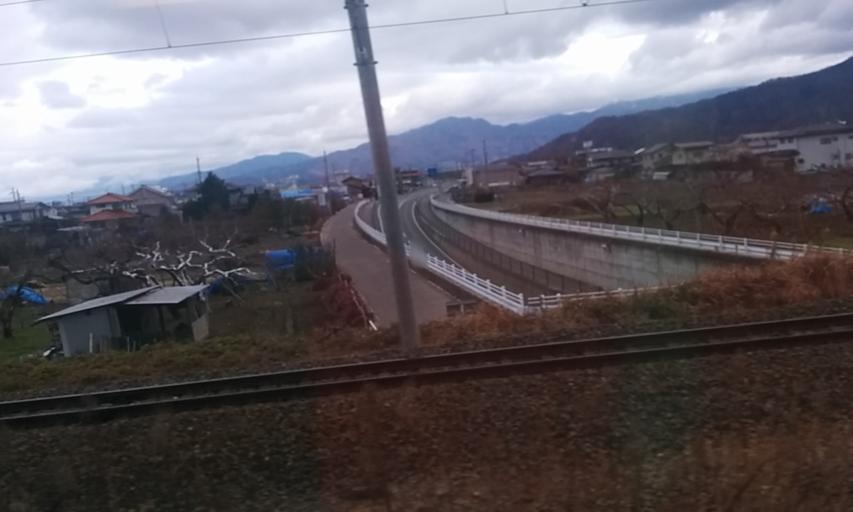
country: JP
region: Nagano
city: Nagano-shi
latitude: 36.5620
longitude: 138.1328
